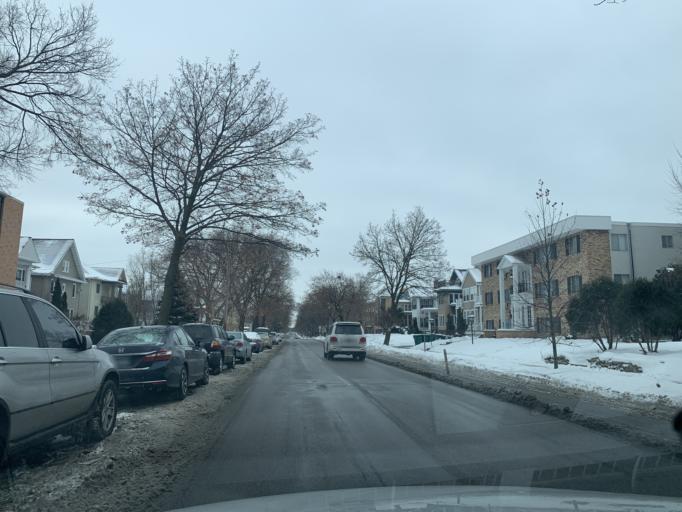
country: US
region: Minnesota
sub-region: Hennepin County
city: Minneapolis
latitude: 44.9585
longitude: -93.2796
